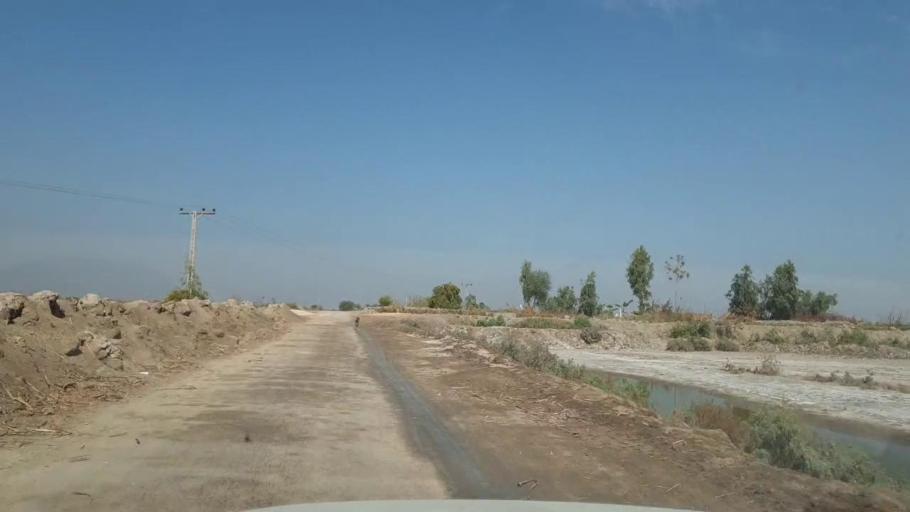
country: PK
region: Sindh
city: Pithoro
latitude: 25.5591
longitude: 69.2098
